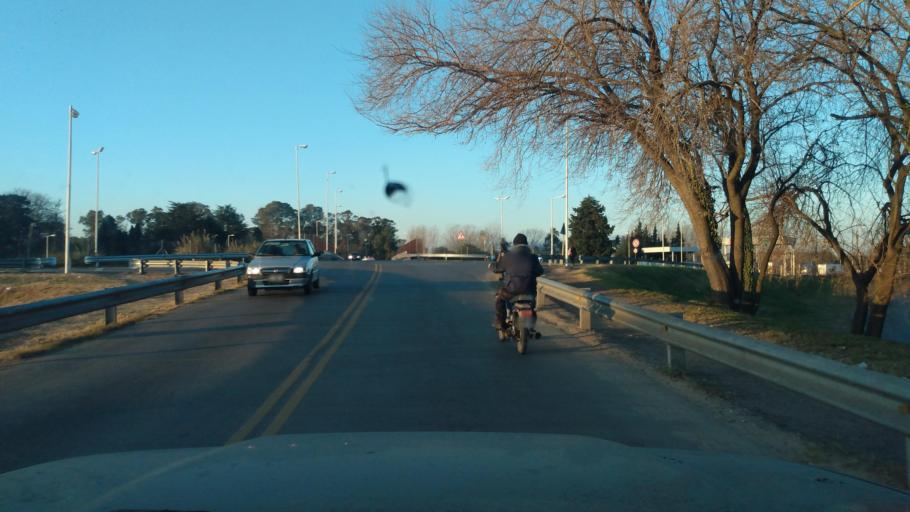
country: AR
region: Buenos Aires
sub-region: Partido de General Rodriguez
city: General Rodriguez
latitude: -34.5965
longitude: -58.9375
